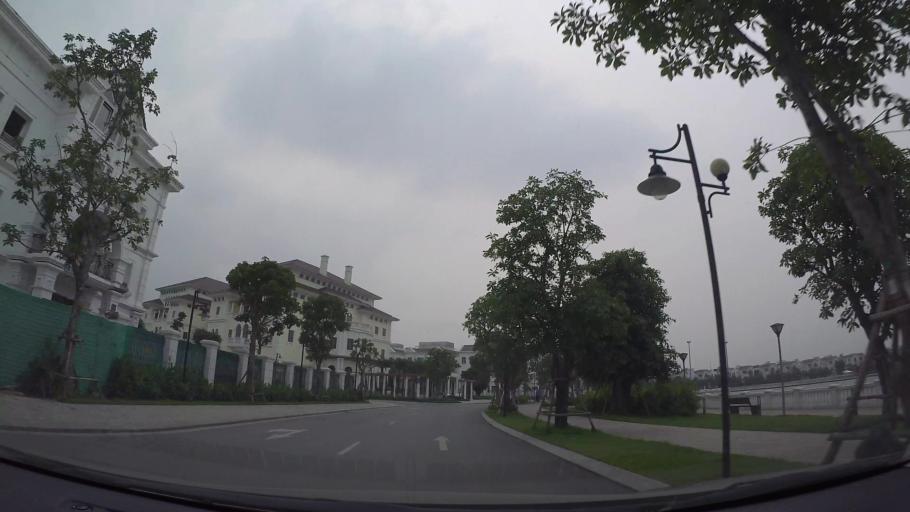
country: VN
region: Ha Noi
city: Trau Quy
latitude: 21.0464
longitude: 105.9059
